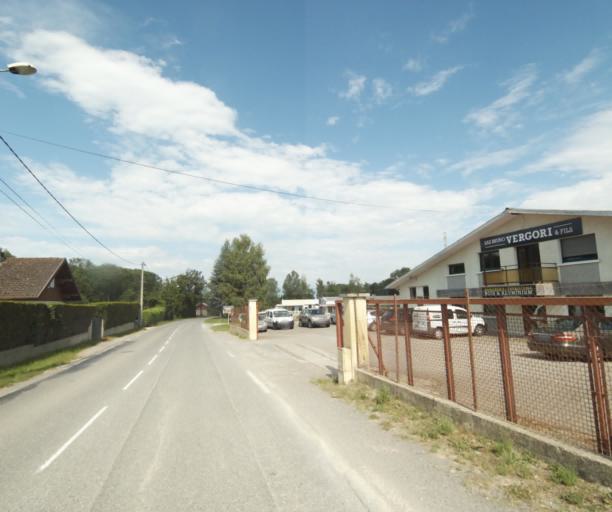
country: FR
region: Rhone-Alpes
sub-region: Departement de la Haute-Savoie
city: Allinges
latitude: 46.3347
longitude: 6.4867
